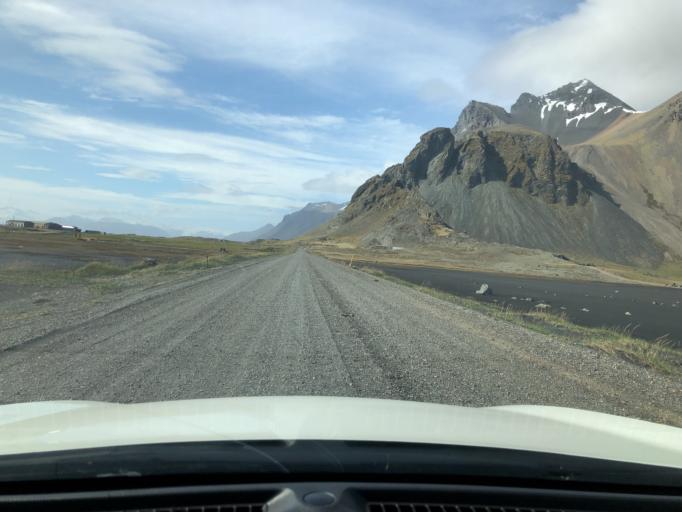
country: IS
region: East
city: Hoefn
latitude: 64.2509
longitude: -14.9867
